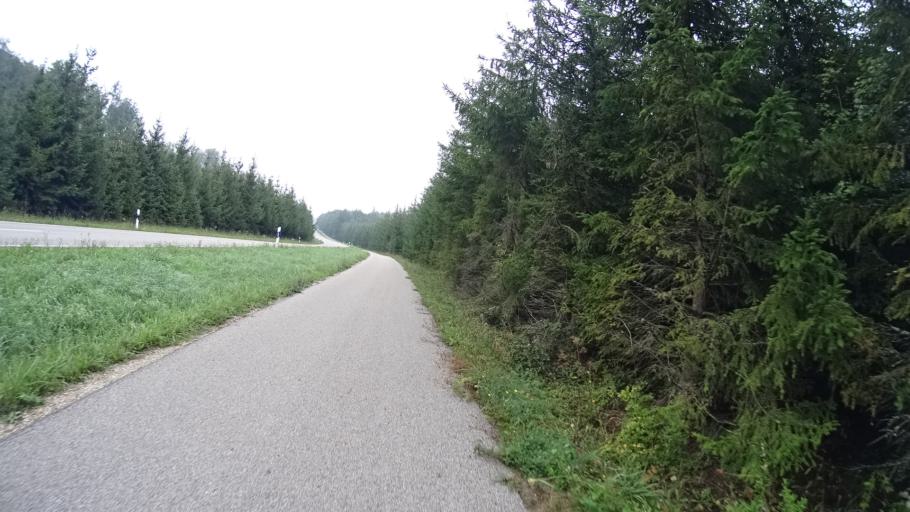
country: DE
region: Bavaria
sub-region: Upper Bavaria
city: Denkendorf
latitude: 48.9064
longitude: 11.4575
